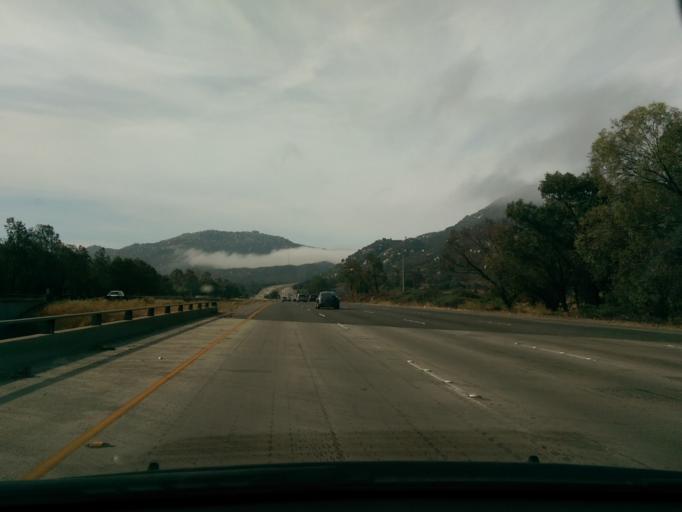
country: US
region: California
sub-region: Riverside County
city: Temecula
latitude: 33.4808
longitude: -117.1410
